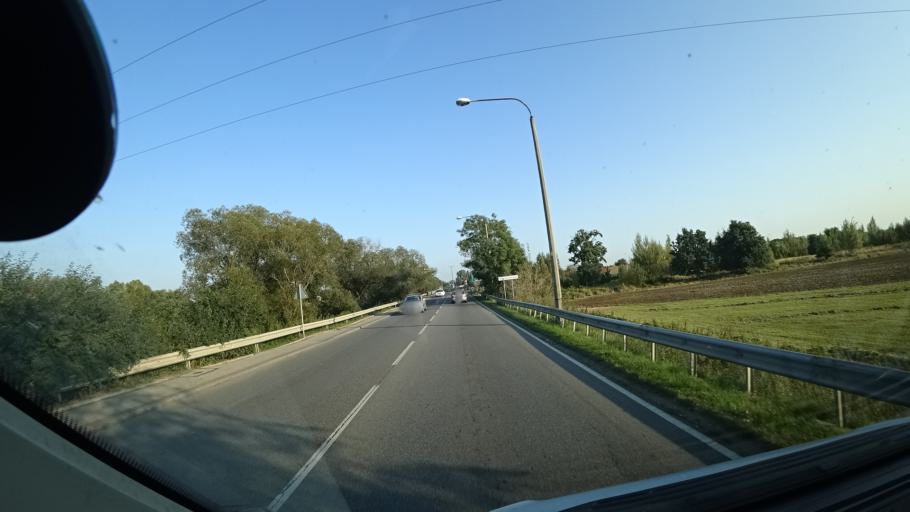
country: PL
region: Opole Voivodeship
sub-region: Powiat kedzierzynsko-kozielski
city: Kozle
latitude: 50.3385
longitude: 18.1791
